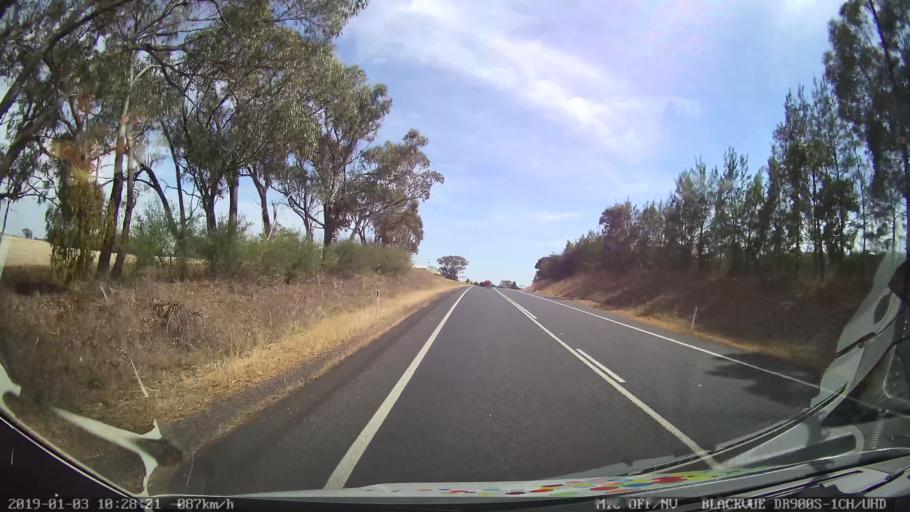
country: AU
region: New South Wales
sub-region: Young
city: Young
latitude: -34.3890
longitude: 148.2586
